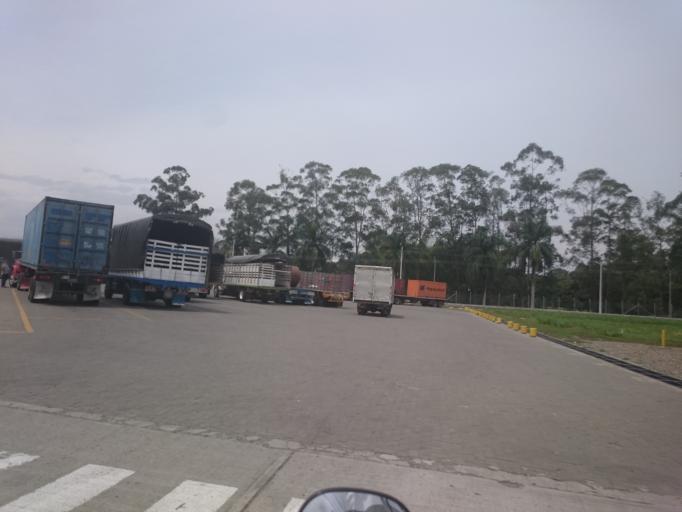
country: CO
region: Cauca
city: Puerto Tejada
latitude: 3.2128
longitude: -76.4262
